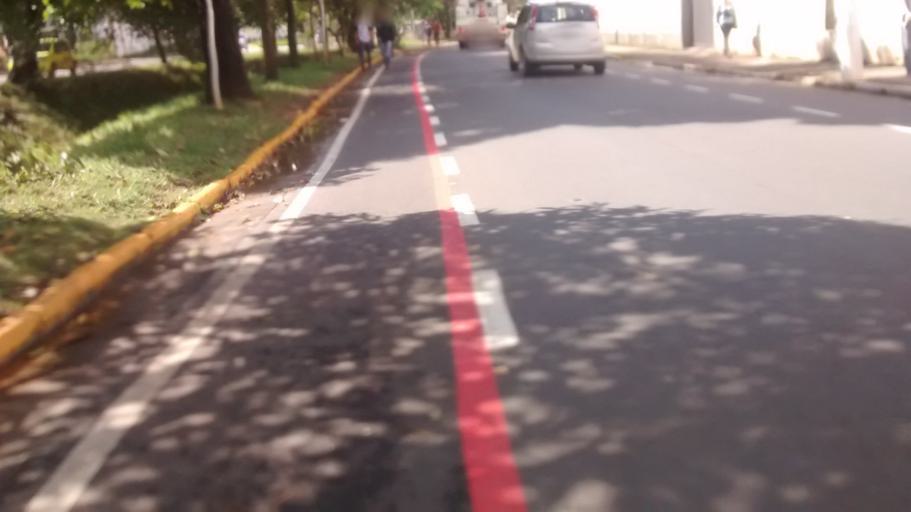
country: BR
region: Minas Gerais
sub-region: Itajuba
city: Itajuba
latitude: -22.4140
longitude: -45.4520
